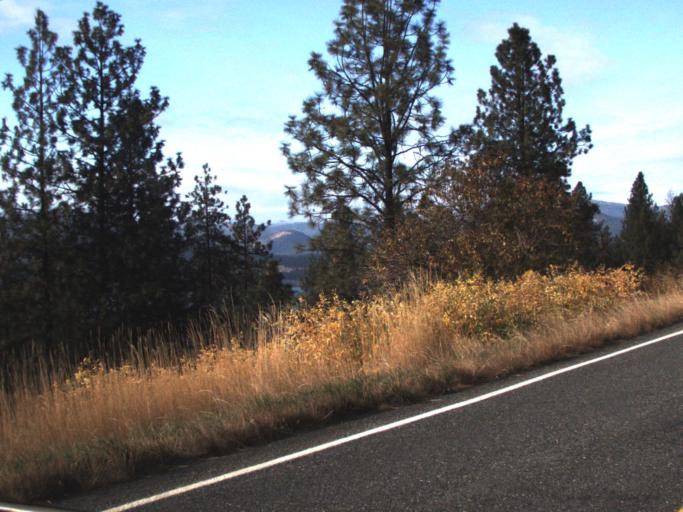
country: US
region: Washington
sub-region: Stevens County
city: Kettle Falls
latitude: 48.3831
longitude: -118.1667
